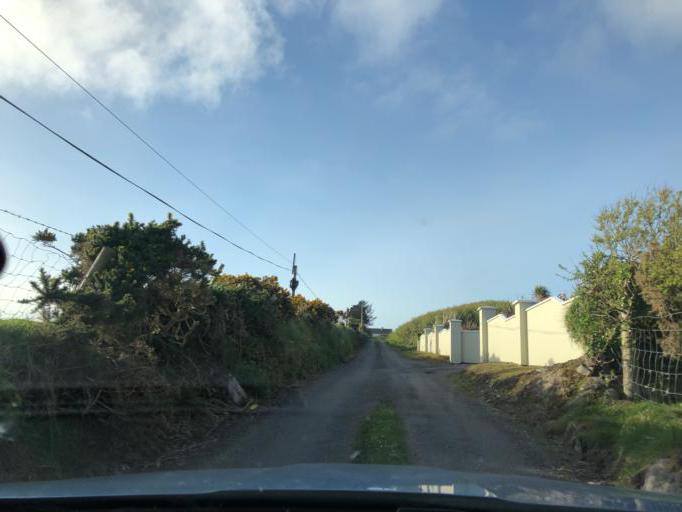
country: IE
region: Munster
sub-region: Ciarrai
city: Cahersiveen
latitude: 51.9581
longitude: -10.2551
